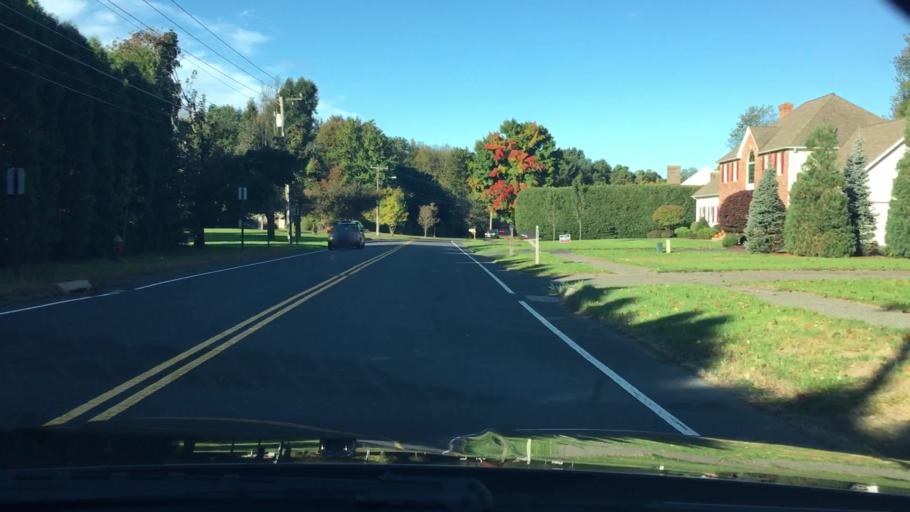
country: US
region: Massachusetts
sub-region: Hampden County
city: East Longmeadow
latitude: 42.0381
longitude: -72.5373
